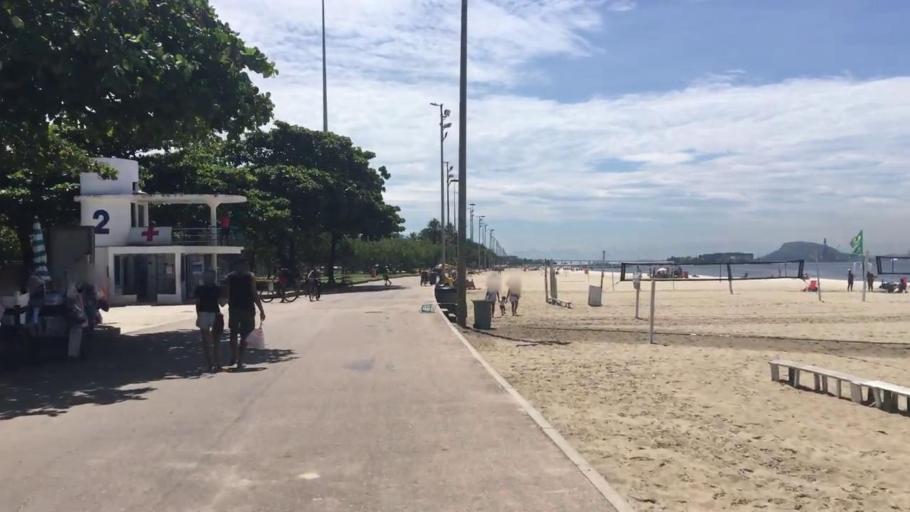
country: BR
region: Rio de Janeiro
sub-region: Rio De Janeiro
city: Rio de Janeiro
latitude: -22.9299
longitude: -43.1717
